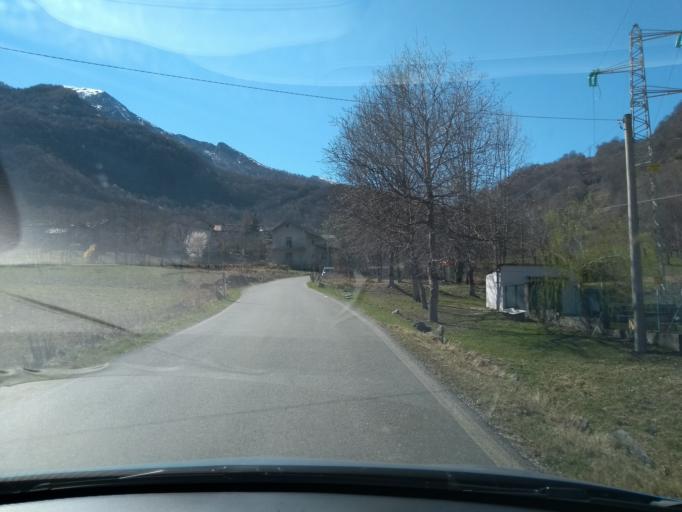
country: IT
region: Piedmont
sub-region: Provincia di Torino
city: Lemie
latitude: 45.2270
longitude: 7.2683
